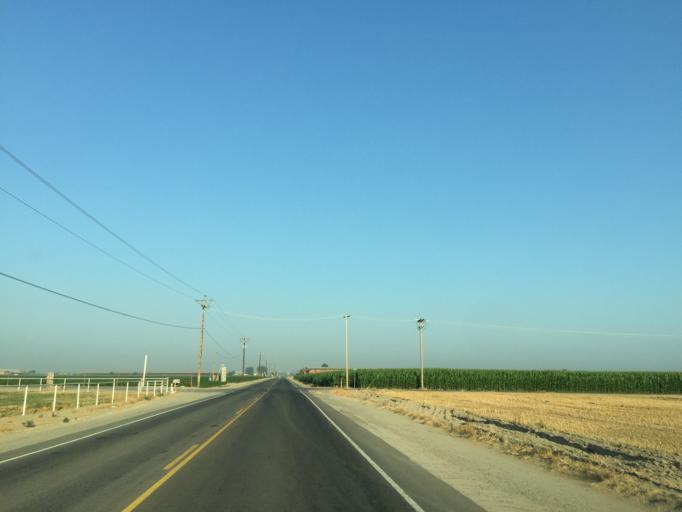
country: US
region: California
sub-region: Tulare County
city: London
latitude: 36.4585
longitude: -119.3847
